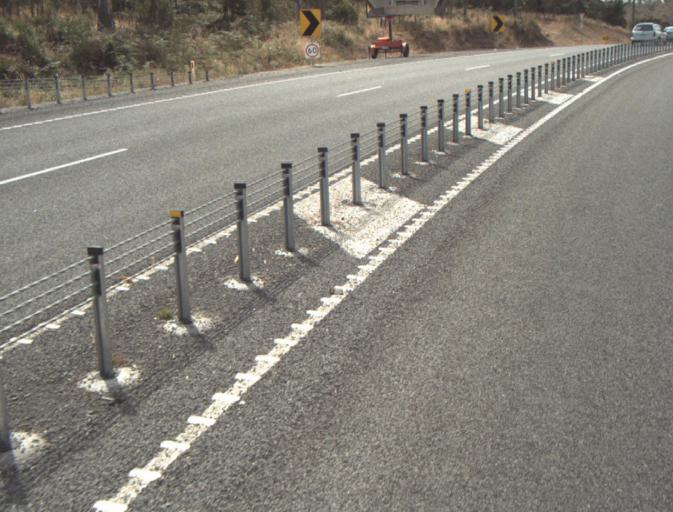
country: AU
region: Tasmania
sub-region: Launceston
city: Mayfield
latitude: -41.2992
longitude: 147.0493
